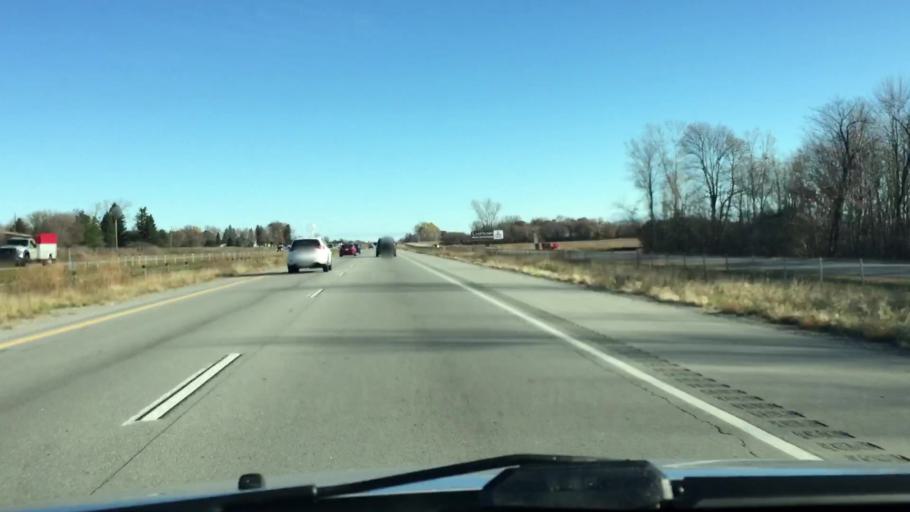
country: US
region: Wisconsin
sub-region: Brown County
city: Wrightstown
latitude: 44.4012
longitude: -88.1491
